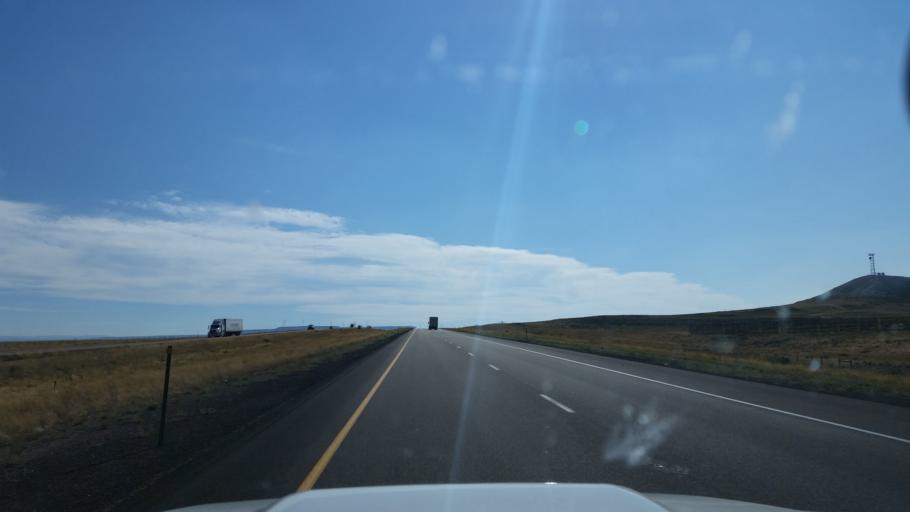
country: US
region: Wyoming
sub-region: Uinta County
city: Lyman
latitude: 41.3504
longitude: -110.3802
